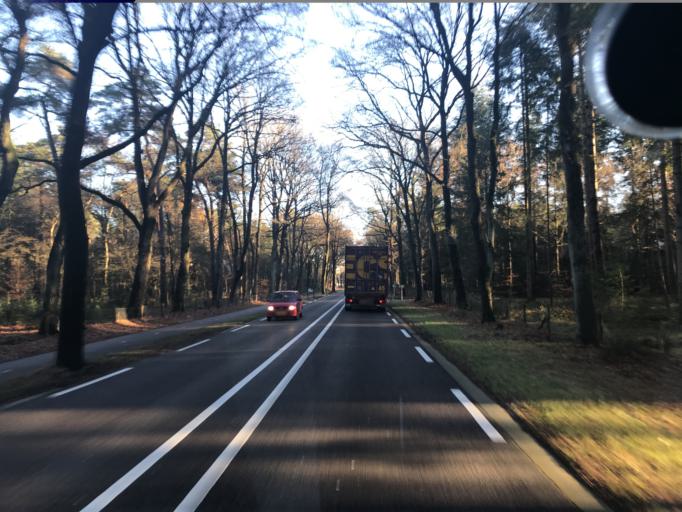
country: NL
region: Gelderland
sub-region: Gemeente Ermelo
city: Ermelo
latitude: 52.3157
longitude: 5.6684
